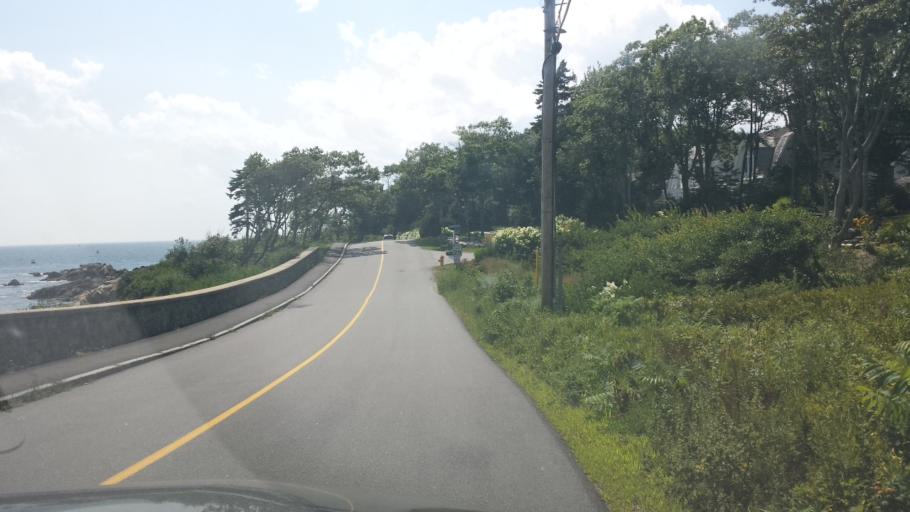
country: US
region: Maine
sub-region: York County
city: Kennebunkport
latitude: 43.3441
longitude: -70.4632
